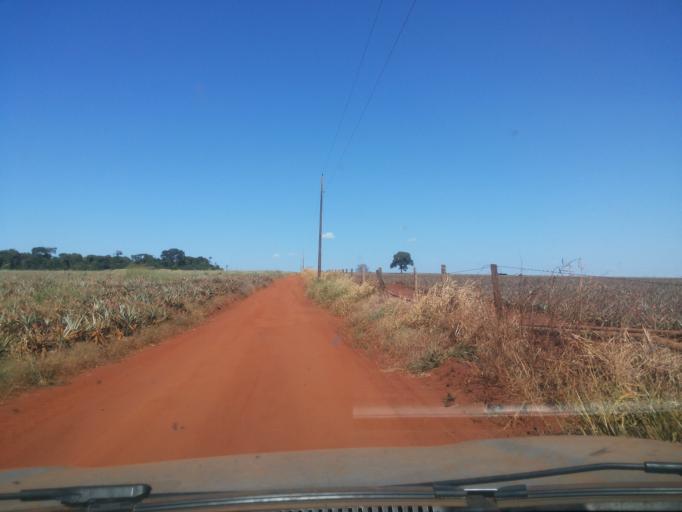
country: BR
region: Minas Gerais
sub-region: Centralina
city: Centralina
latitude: -18.7415
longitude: -49.1896
